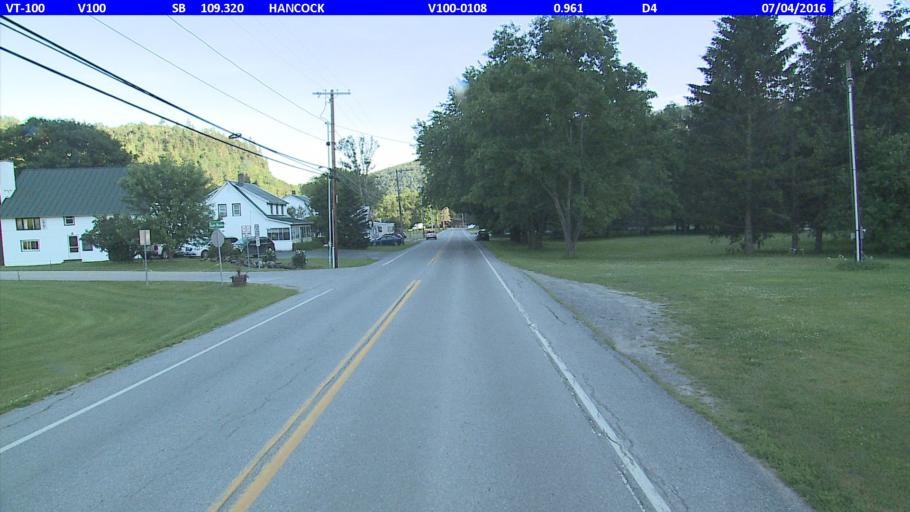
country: US
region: Vermont
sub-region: Orange County
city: Randolph
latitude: 43.9227
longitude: -72.8405
